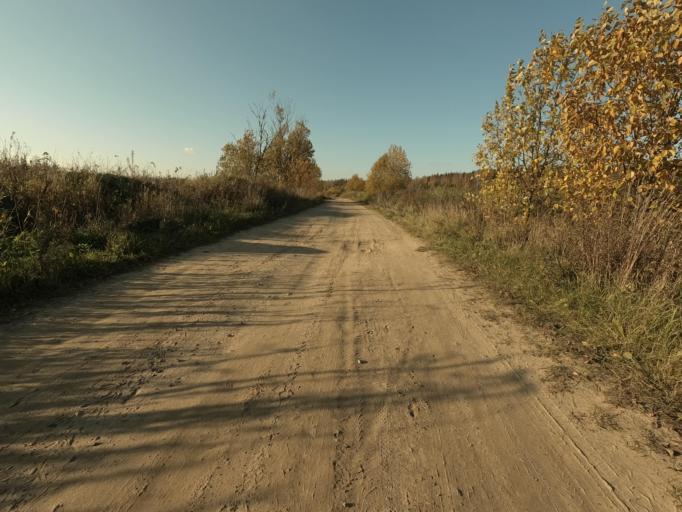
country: RU
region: Leningrad
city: Luppolovo
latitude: 60.1436
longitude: 30.2475
